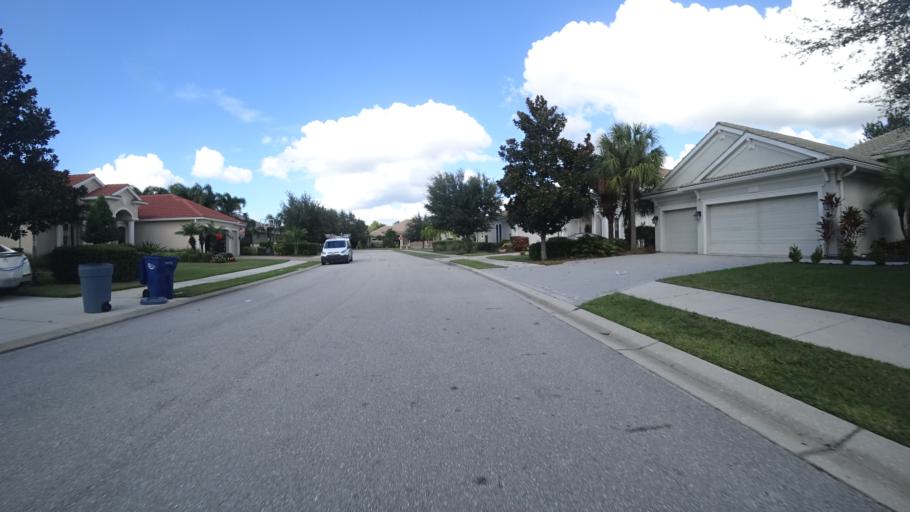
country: US
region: Florida
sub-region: Sarasota County
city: The Meadows
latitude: 27.4218
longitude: -82.3919
